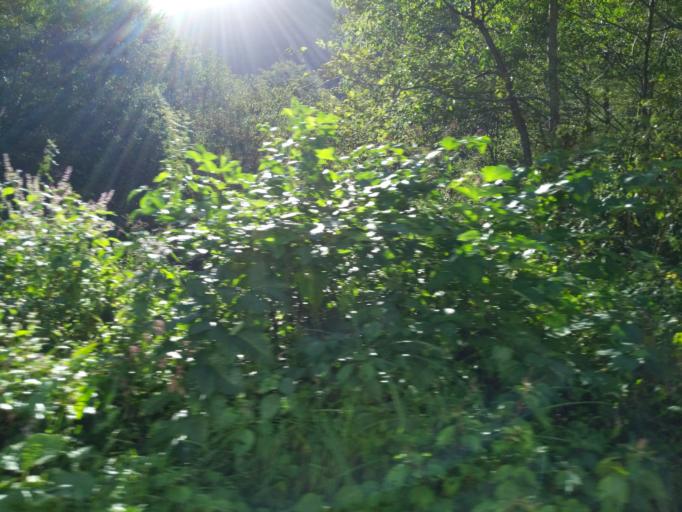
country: JP
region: Toyama
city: Kamiichi
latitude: 36.5158
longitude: 137.4501
